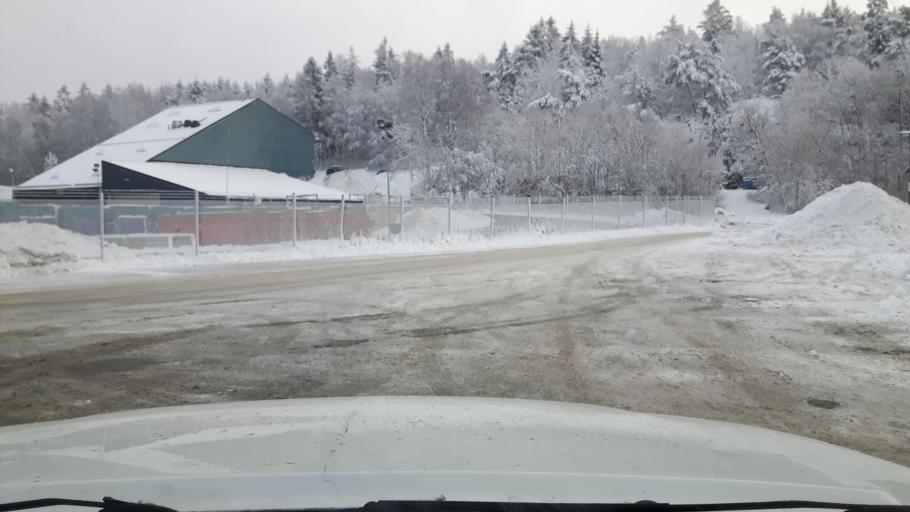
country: SE
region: Halland
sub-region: Kungsbacka Kommun
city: Kungsbacka
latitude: 57.4877
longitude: 12.0490
